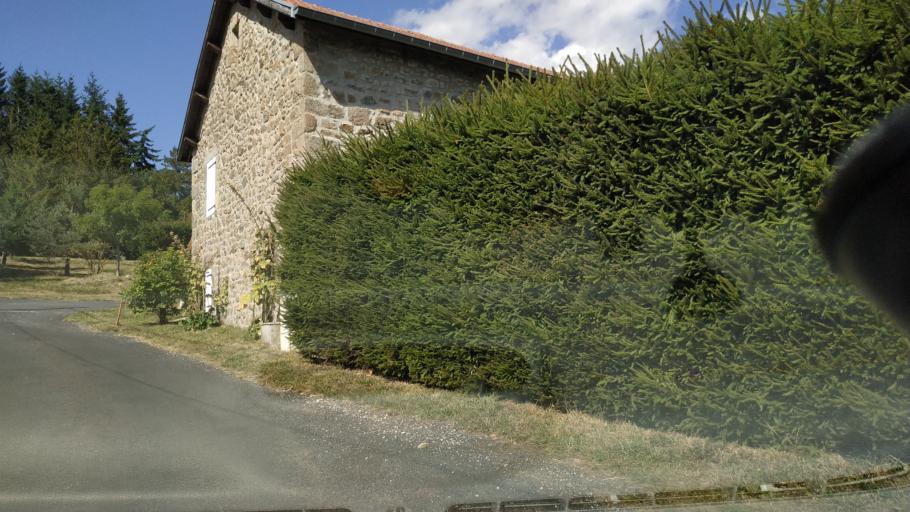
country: FR
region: Rhone-Alpes
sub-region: Departement de l'Ardeche
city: Saint-Agreve
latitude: 45.0281
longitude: 4.4429
